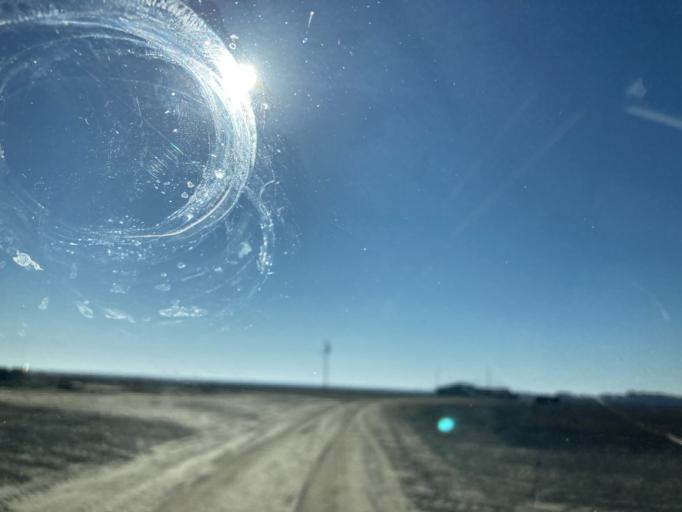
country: US
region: Mississippi
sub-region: Sharkey County
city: Rolling Fork
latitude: 32.8685
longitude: -90.6926
